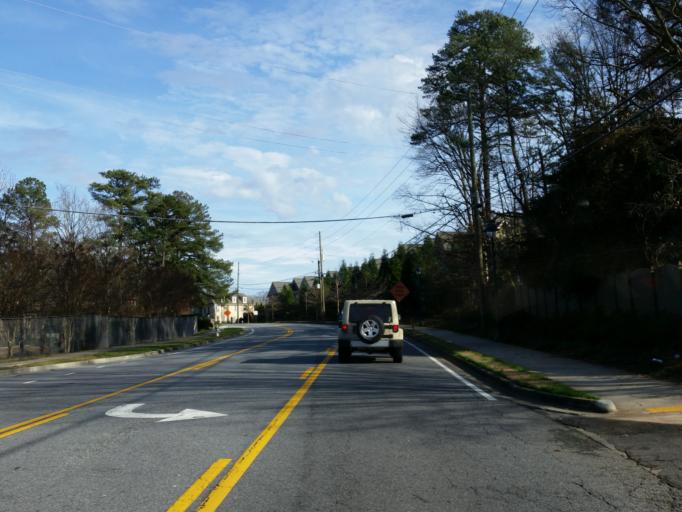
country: US
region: Georgia
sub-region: DeKalb County
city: Dunwoody
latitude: 33.9550
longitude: -84.3634
